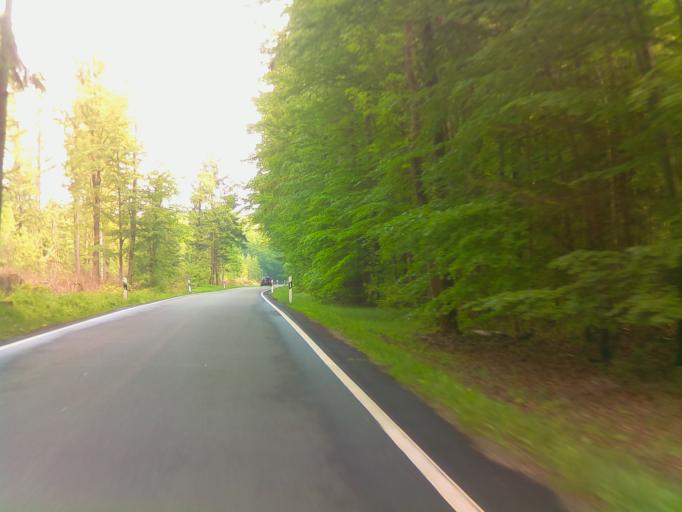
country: DE
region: Hesse
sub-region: Regierungsbezirk Darmstadt
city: Lutzelbach
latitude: 49.7272
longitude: 9.0850
